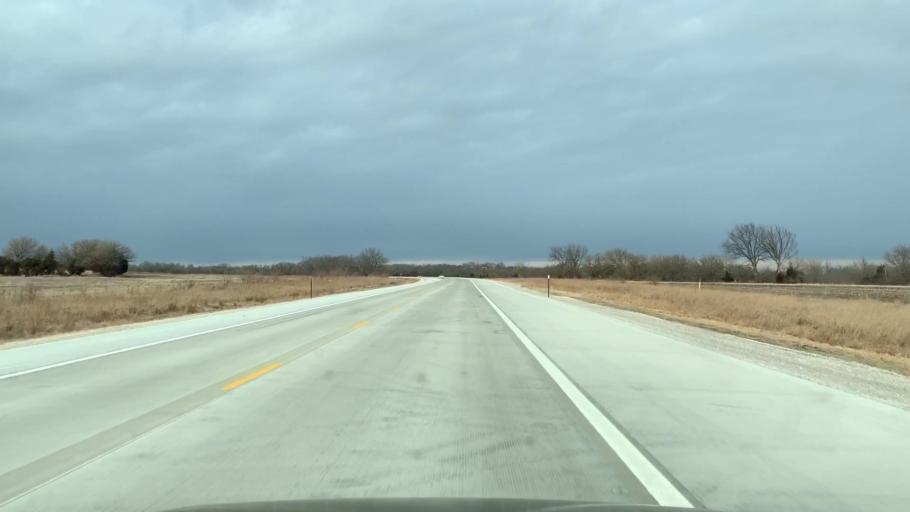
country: US
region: Kansas
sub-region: Allen County
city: Humboldt
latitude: 37.8584
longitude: -95.4066
